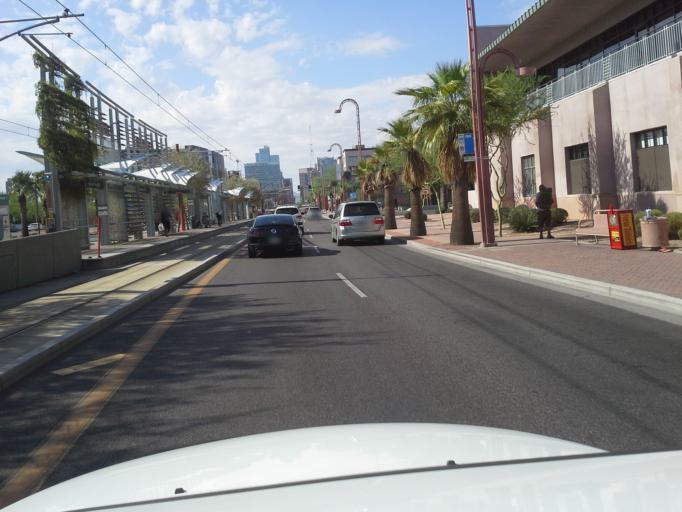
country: US
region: Arizona
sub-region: Maricopa County
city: Phoenix
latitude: 33.4654
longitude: -112.0739
